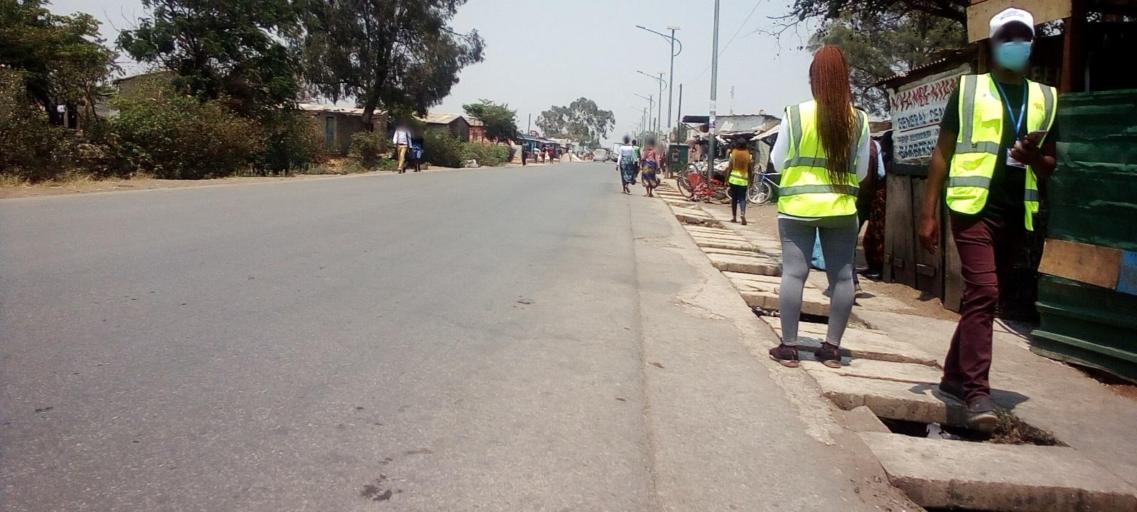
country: ZM
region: Lusaka
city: Lusaka
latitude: -15.4386
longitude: 28.2557
